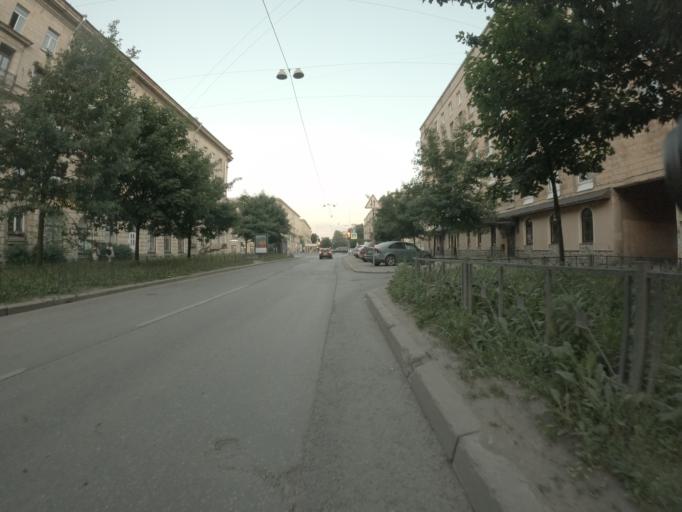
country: RU
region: St.-Petersburg
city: Centralniy
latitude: 59.9286
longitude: 30.4065
